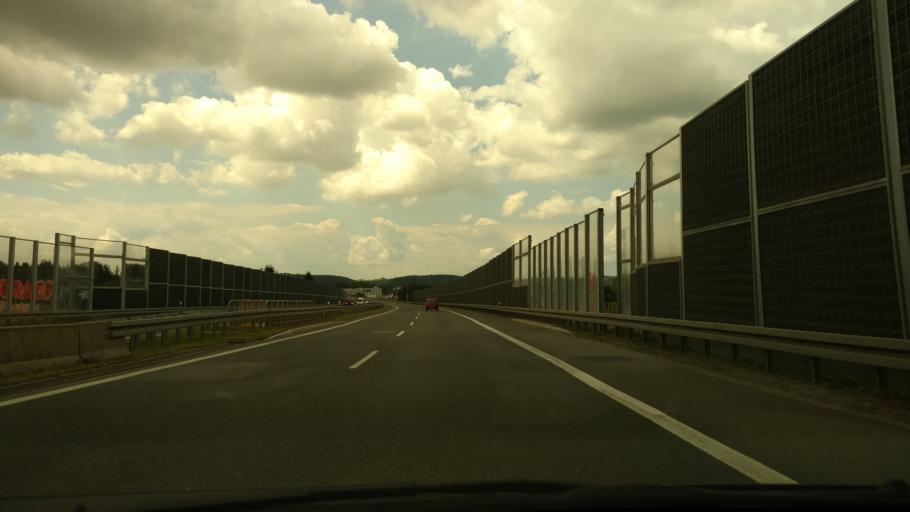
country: PL
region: Lesser Poland Voivodeship
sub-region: Powiat krakowski
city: Modlniczka
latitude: 50.1171
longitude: 19.8557
